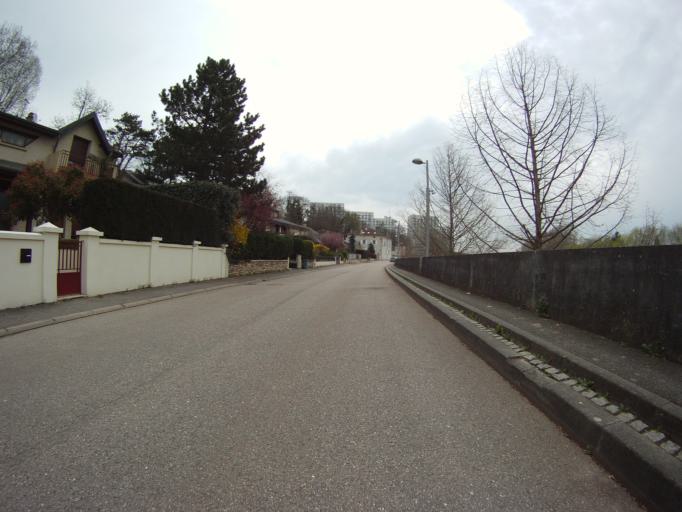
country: FR
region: Lorraine
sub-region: Departement de Meurthe-et-Moselle
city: Malzeville
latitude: 48.7056
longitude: 6.1876
